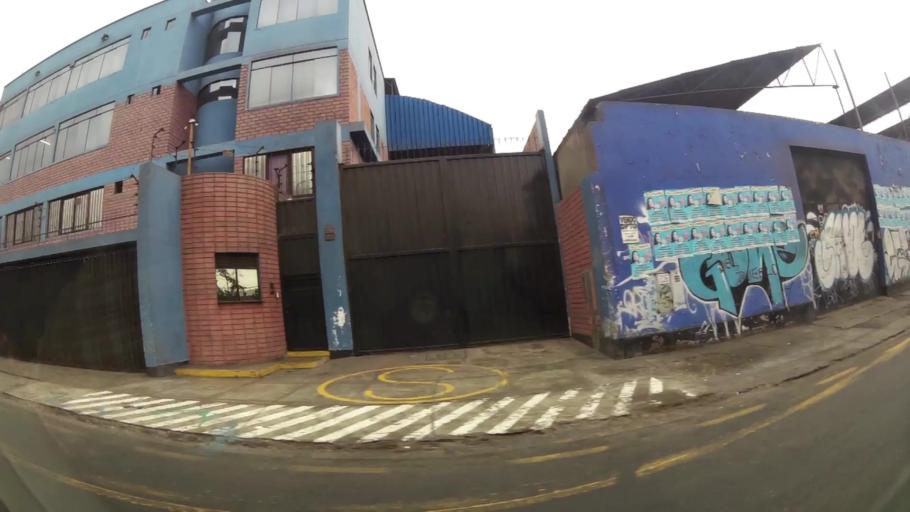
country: PE
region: Lima
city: Lima
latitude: -12.0502
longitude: -77.0542
